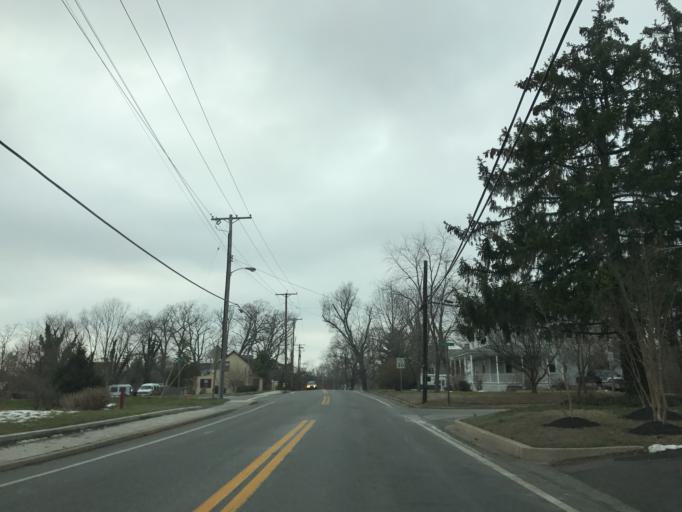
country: US
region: Maryland
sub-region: Harford County
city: Aberdeen
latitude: 39.5141
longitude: -76.1758
